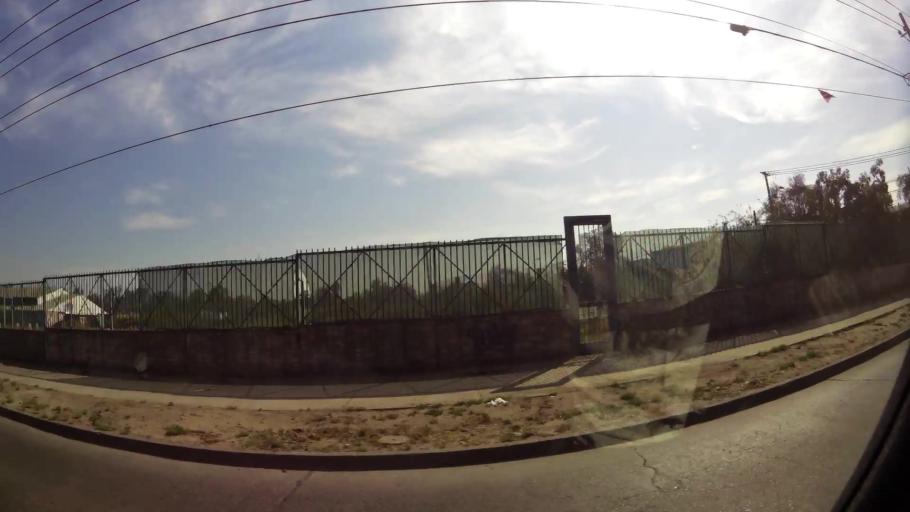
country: CL
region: Santiago Metropolitan
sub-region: Provincia de Santiago
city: Lo Prado
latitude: -33.4501
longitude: -70.7397
